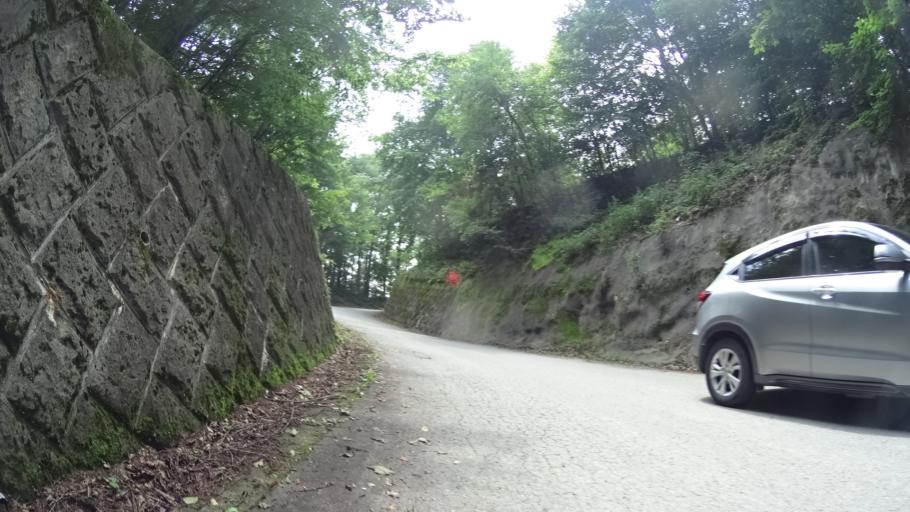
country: JP
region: Nagano
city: Saku
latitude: 36.0986
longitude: 138.6707
